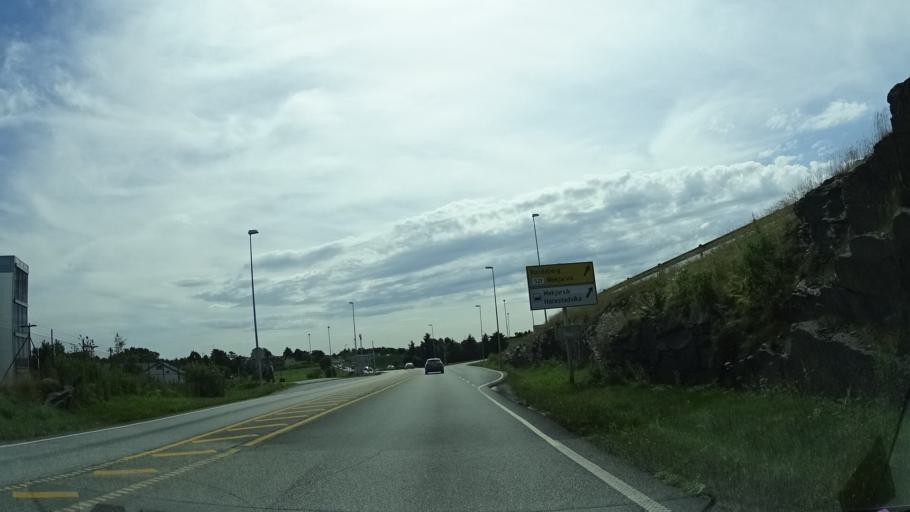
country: NO
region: Rogaland
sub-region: Randaberg
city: Randaberg
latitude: 59.0135
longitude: 5.6348
